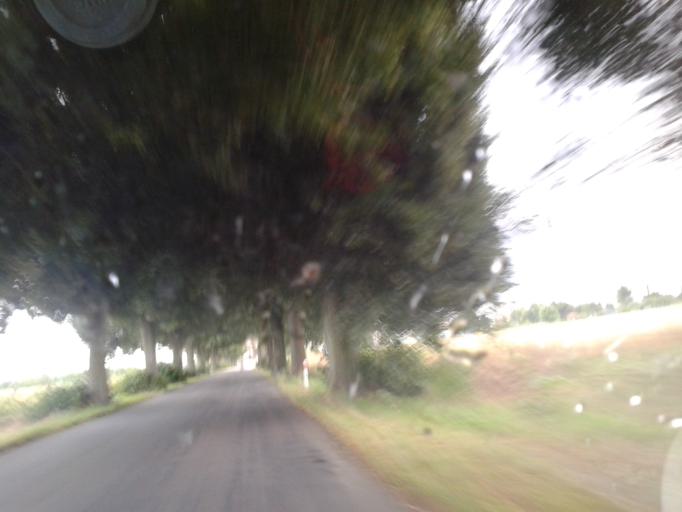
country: PL
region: West Pomeranian Voivodeship
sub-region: Powiat szczecinecki
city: Grzmiaca
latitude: 53.8411
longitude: 16.4424
